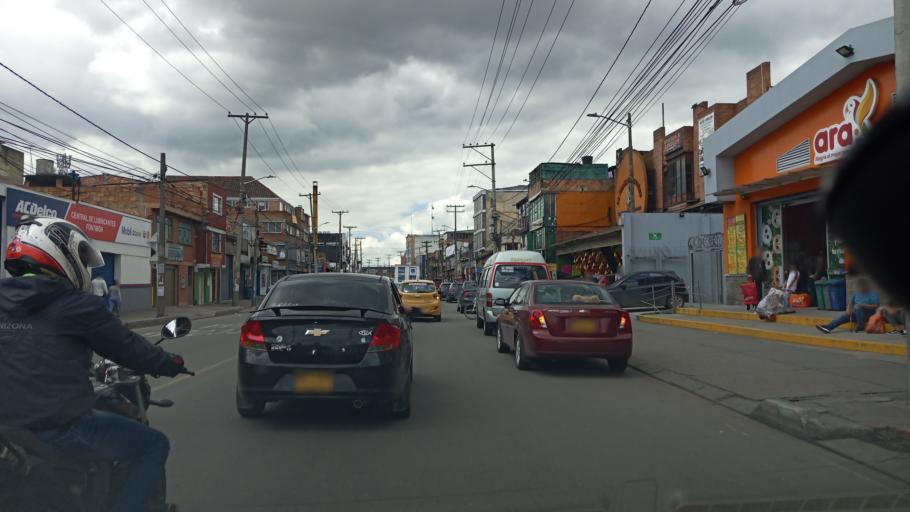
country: CO
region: Cundinamarca
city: Funza
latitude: 4.6708
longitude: -74.1441
